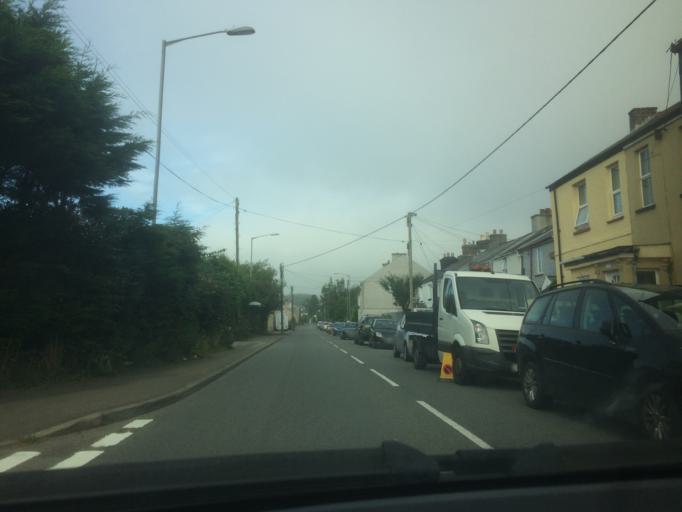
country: GB
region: England
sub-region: Cornwall
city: Gunnislake
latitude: 50.5161
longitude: -4.2351
